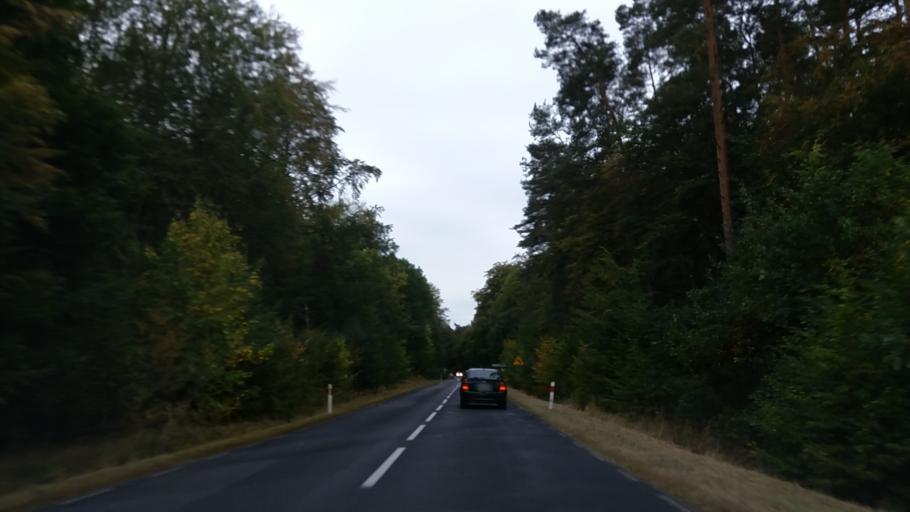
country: PL
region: Lubusz
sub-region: Powiat gorzowski
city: Klodawa
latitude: 52.8453
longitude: 15.2000
